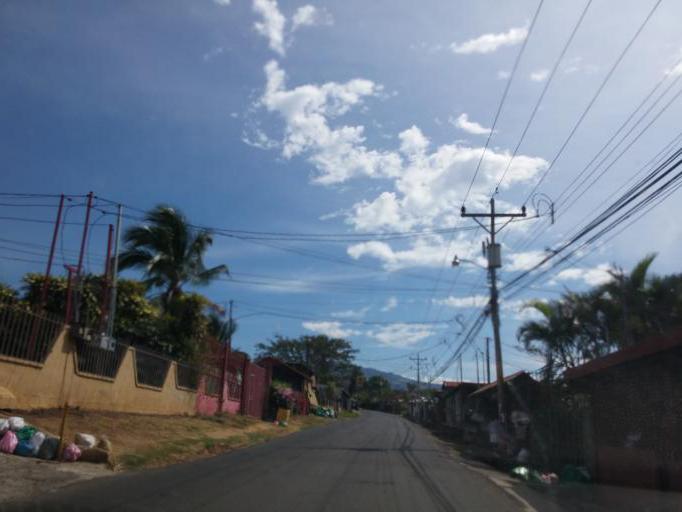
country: CR
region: Alajuela
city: Alajuela
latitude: 10.0415
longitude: -84.2197
